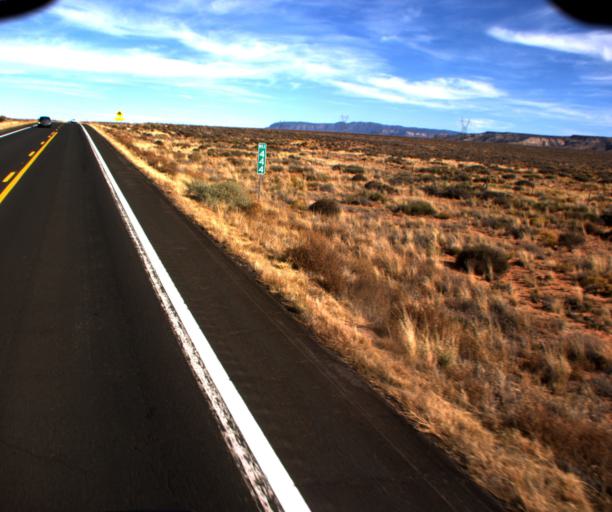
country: US
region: Arizona
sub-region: Apache County
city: Lukachukai
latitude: 36.9634
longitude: -109.4606
